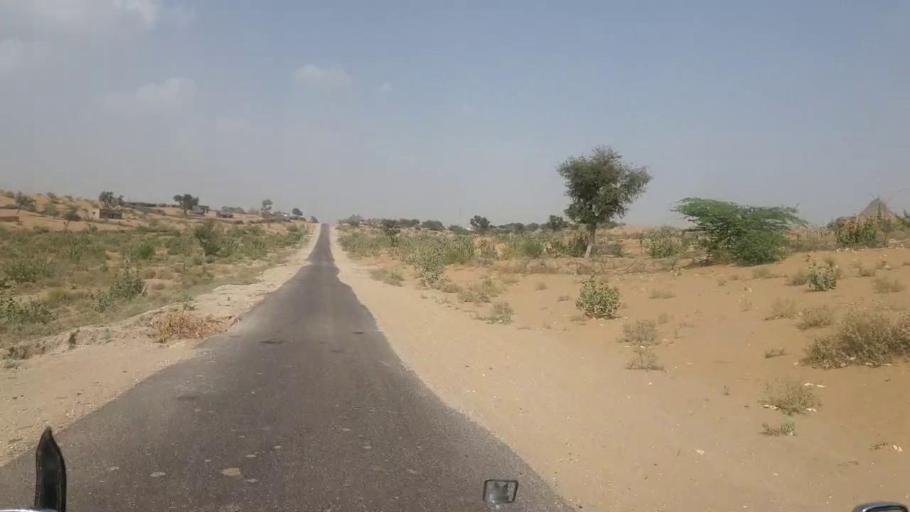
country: PK
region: Sindh
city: Islamkot
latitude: 25.2117
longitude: 70.2836
